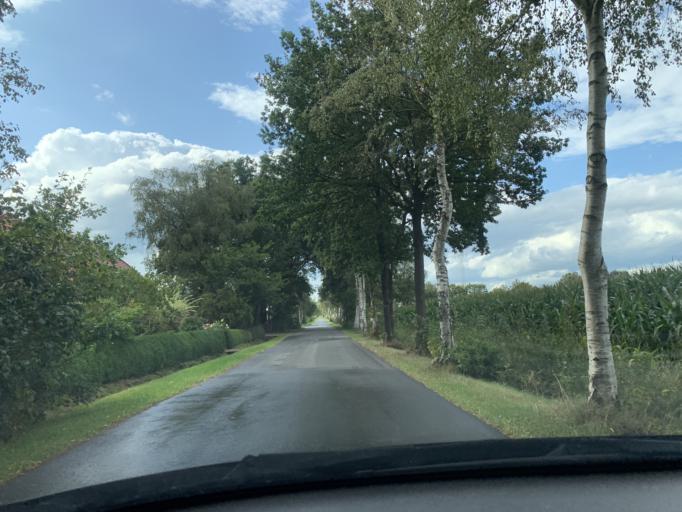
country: DE
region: Lower Saxony
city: Westerstede
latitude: 53.3005
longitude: 8.0120
